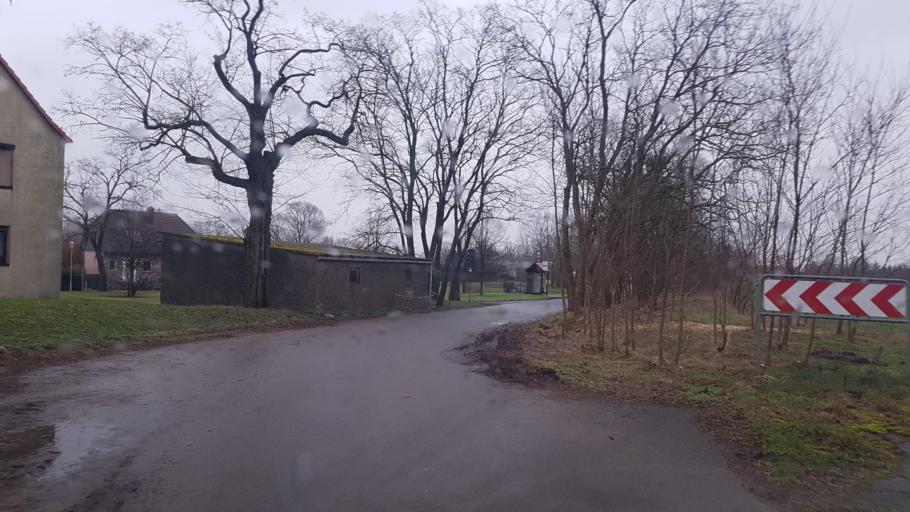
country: DE
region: Brandenburg
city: Zehdenick
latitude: 52.9682
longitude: 13.2772
